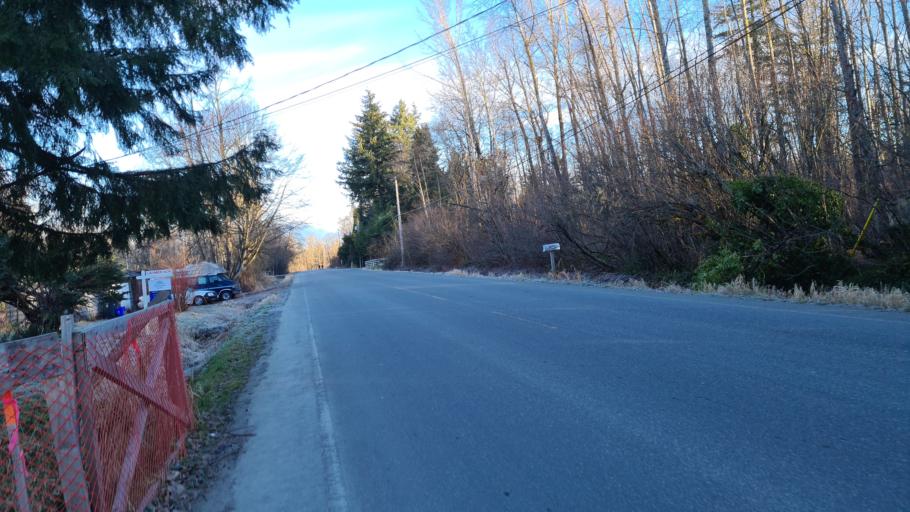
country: CA
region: British Columbia
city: Langley
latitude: 49.1378
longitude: -122.6723
